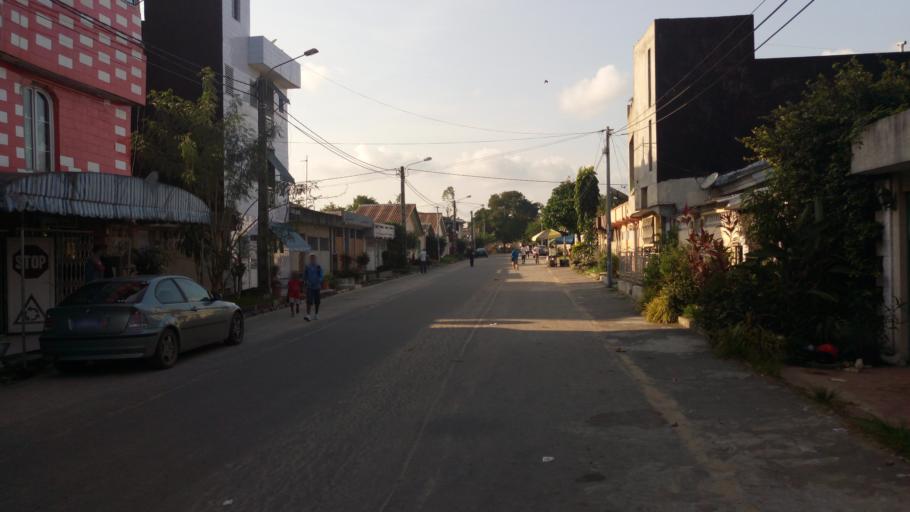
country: CI
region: Lagunes
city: Abobo
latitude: 5.4036
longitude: -3.9806
